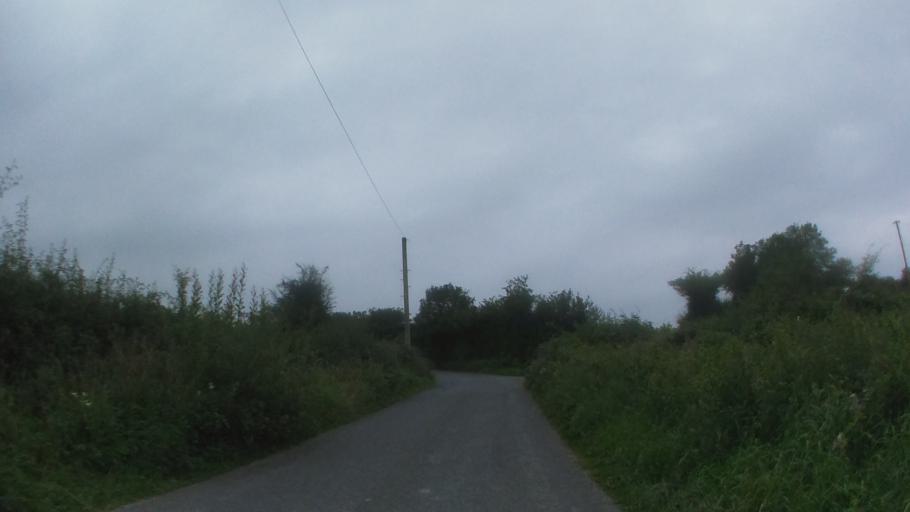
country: IE
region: Leinster
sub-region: Kilkenny
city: Kilkenny
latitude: 52.7003
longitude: -7.1932
